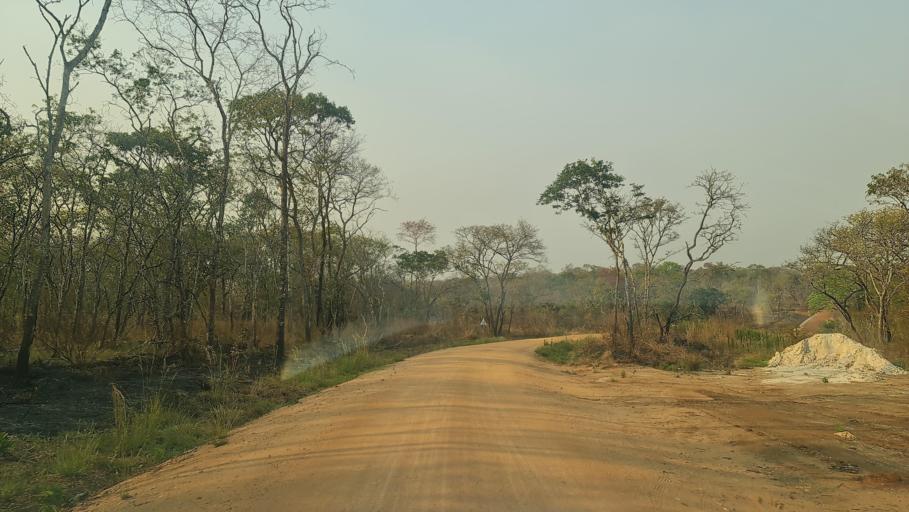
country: MZ
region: Zambezia
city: Quelimane
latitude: -17.1419
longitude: 37.1356
